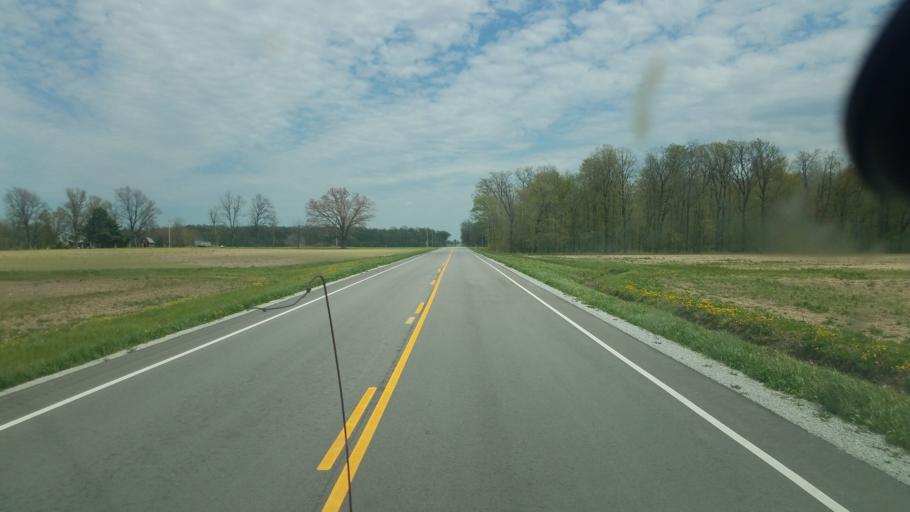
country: US
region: Ohio
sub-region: Hancock County
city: Arlington
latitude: 40.8339
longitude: -83.6367
